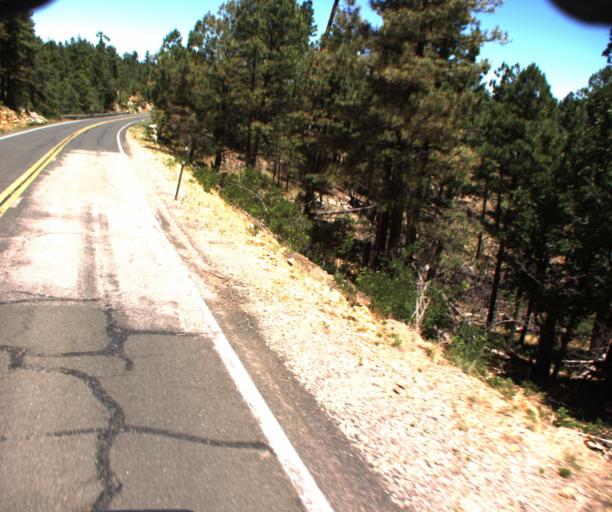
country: US
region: Arizona
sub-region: Gila County
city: Pine
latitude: 34.6012
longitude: -111.2394
